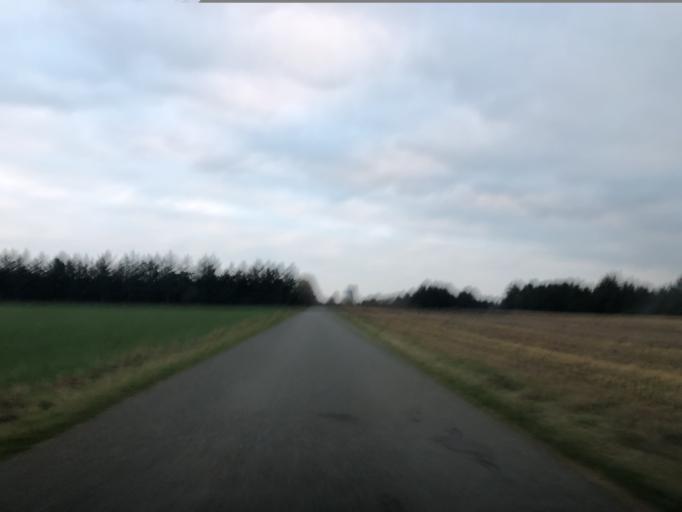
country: DK
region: Central Jutland
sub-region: Holstebro Kommune
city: Ulfborg
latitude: 56.2457
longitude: 8.2832
